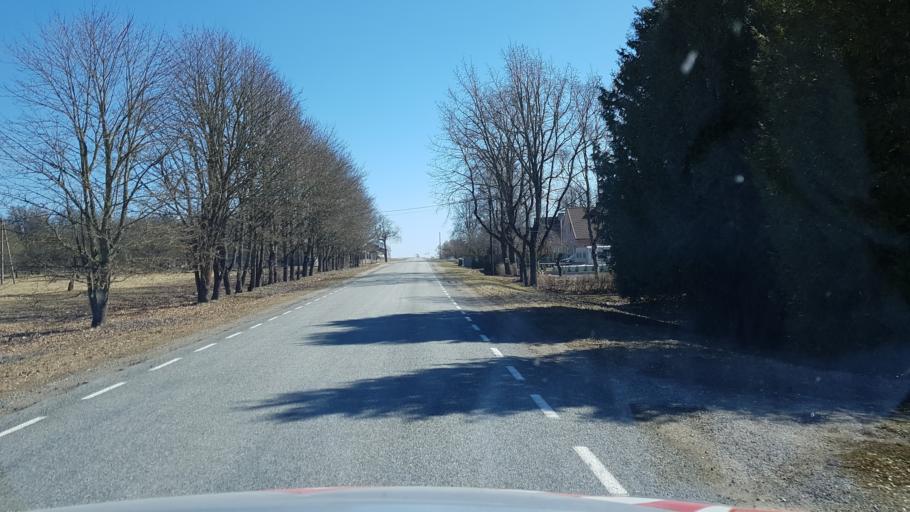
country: EE
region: Laeaene-Virumaa
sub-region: Vaeike-Maarja vald
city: Vaike-Maarja
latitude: 59.1162
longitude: 26.3276
